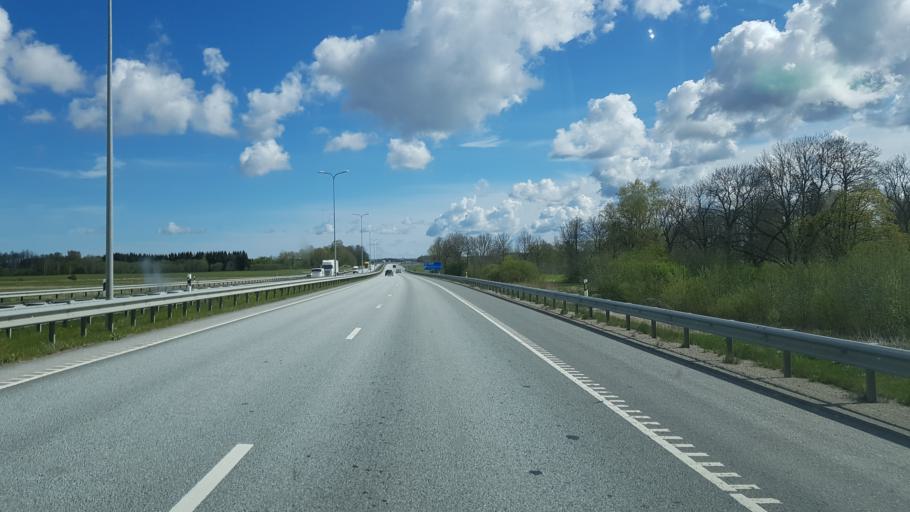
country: EE
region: Harju
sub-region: Kiili vald
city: Kiili
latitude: 59.3398
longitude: 24.8405
